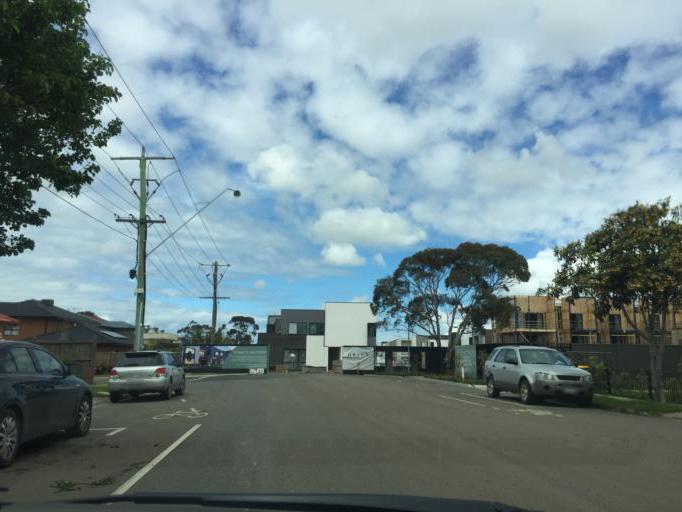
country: AU
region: Victoria
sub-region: Maribyrnong
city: Braybrook
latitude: -37.7936
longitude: 144.8508
